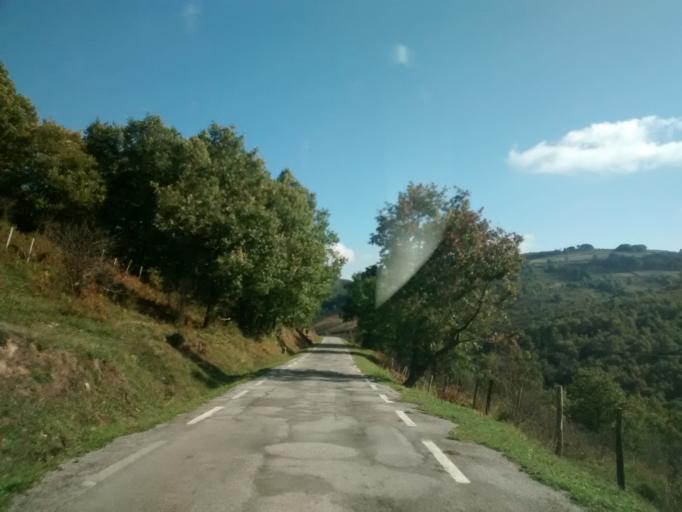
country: ES
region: Castille and Leon
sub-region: Provincia de Burgos
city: Arija
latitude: 42.9287
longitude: -4.0217
